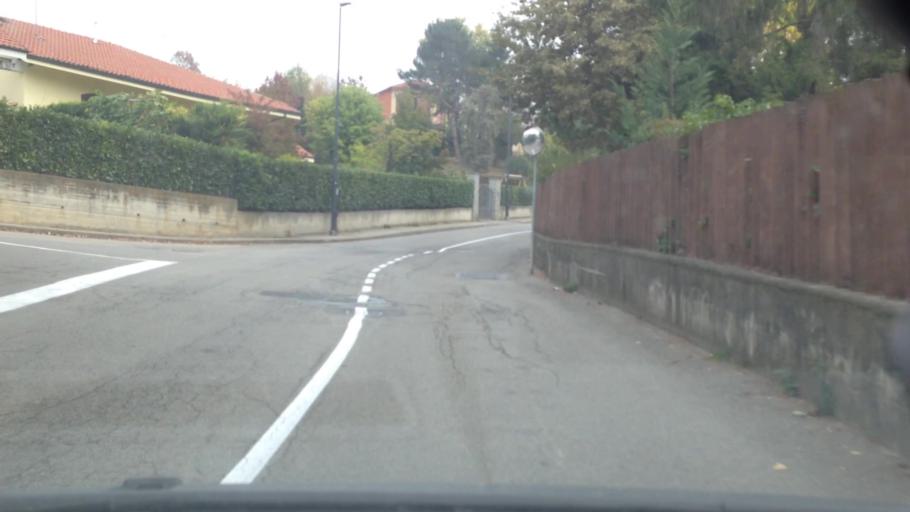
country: IT
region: Piedmont
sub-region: Provincia di Asti
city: Asti
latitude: 44.9155
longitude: 8.1996
